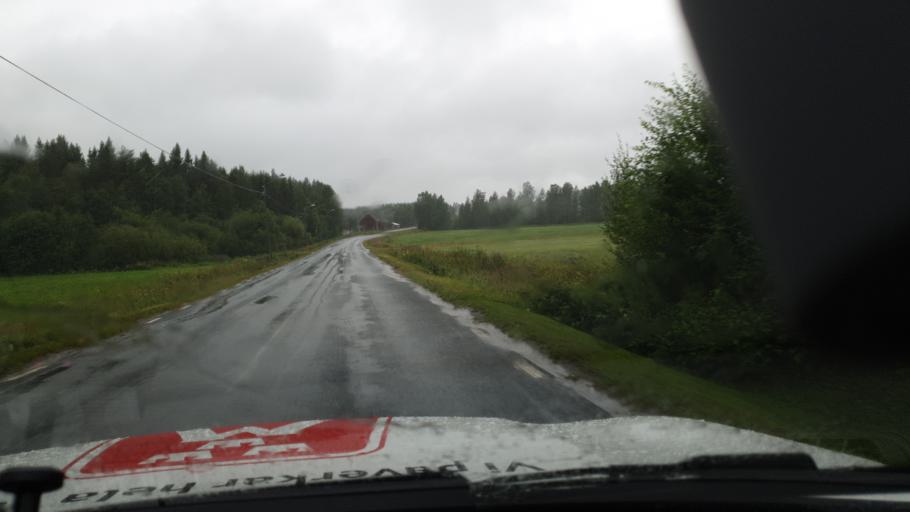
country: SE
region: Vaesterbotten
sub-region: Skelleftea Kommun
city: Viken
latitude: 64.5846
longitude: 20.9611
